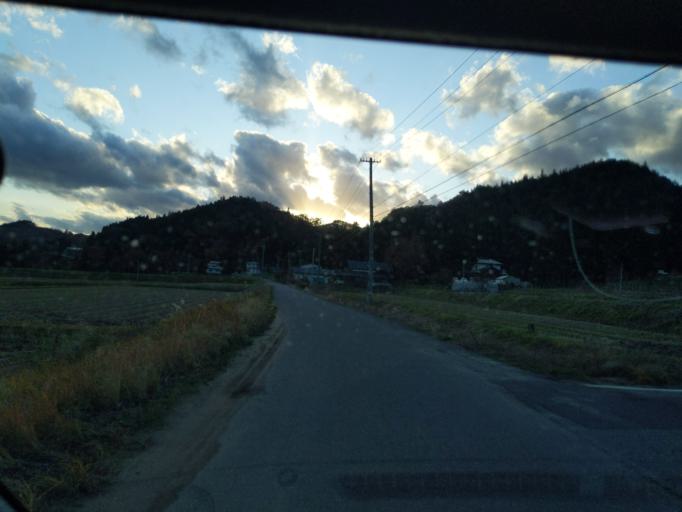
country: JP
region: Iwate
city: Mizusawa
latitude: 39.0321
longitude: 141.0415
